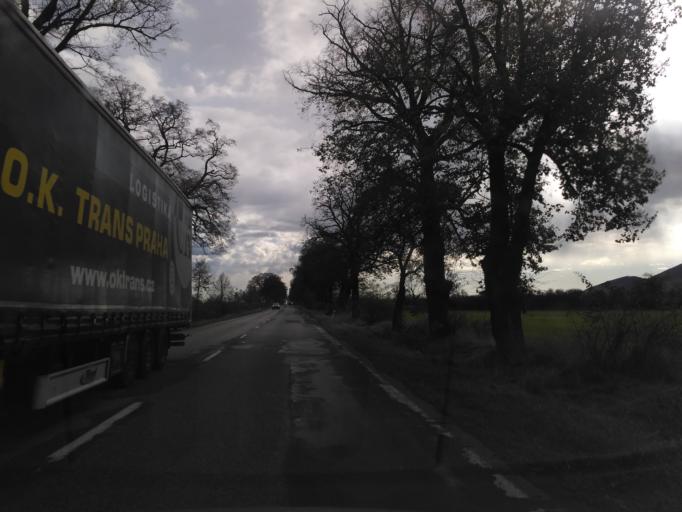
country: HU
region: Borsod-Abauj-Zemplen
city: Satoraljaujhely
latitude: 48.4532
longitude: 21.6480
